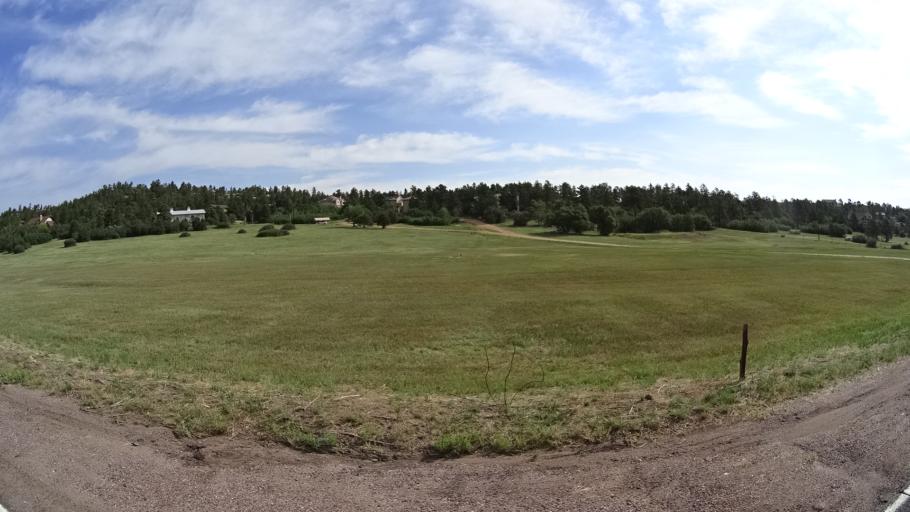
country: US
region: Colorado
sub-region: El Paso County
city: Air Force Academy
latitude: 38.9385
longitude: -104.8328
